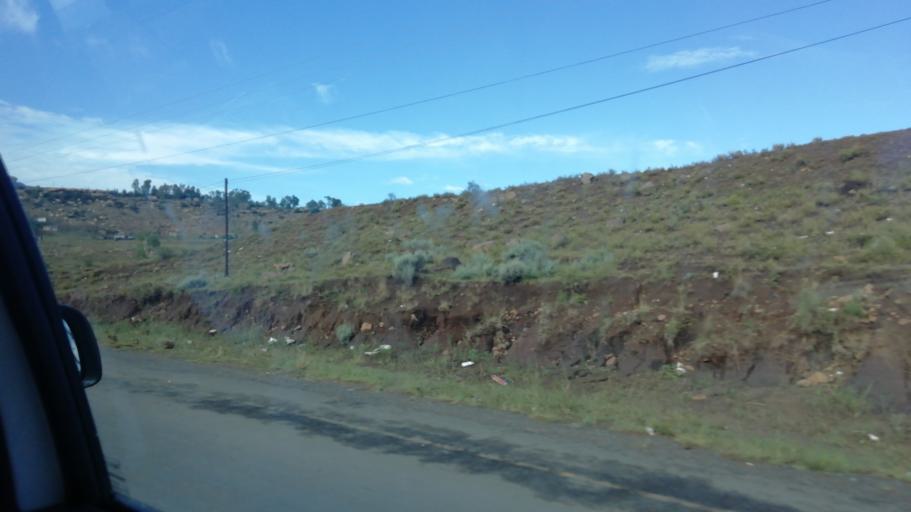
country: LS
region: Maseru
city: Maseru
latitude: -29.3877
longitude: 27.4704
